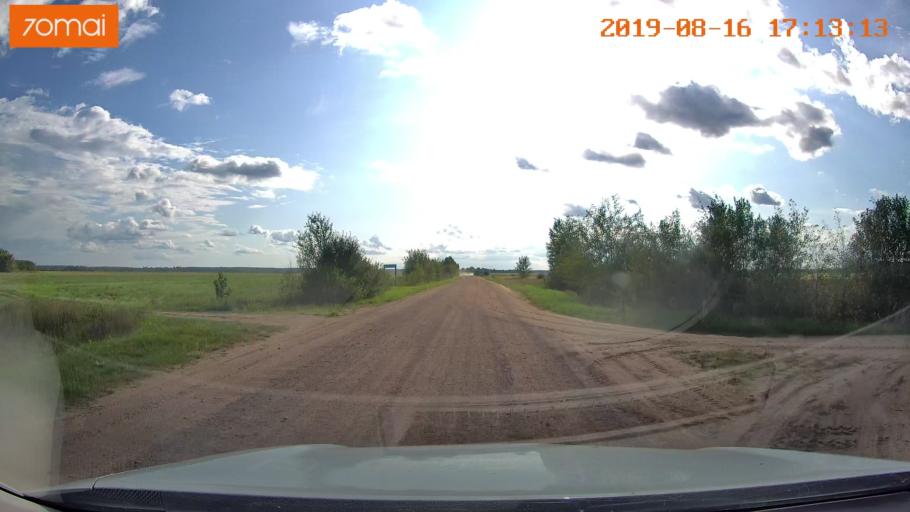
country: BY
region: Mogilev
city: Hlusha
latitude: 53.1910
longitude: 28.8799
